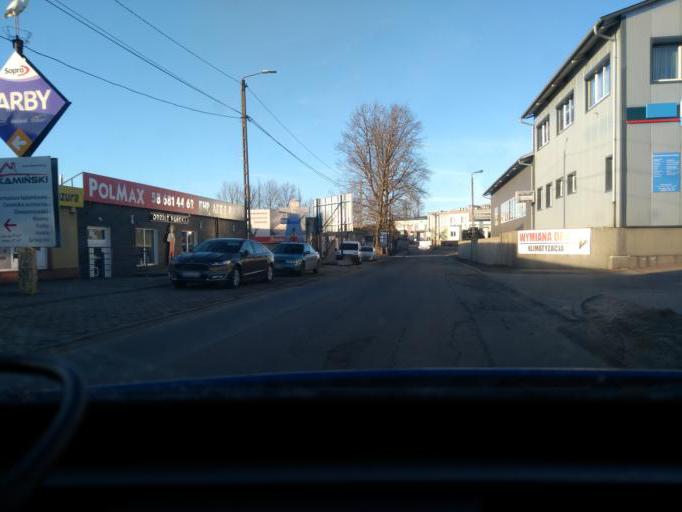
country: PL
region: Pomeranian Voivodeship
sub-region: Powiat kartuski
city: Kartuzy
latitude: 54.3315
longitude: 18.2073
